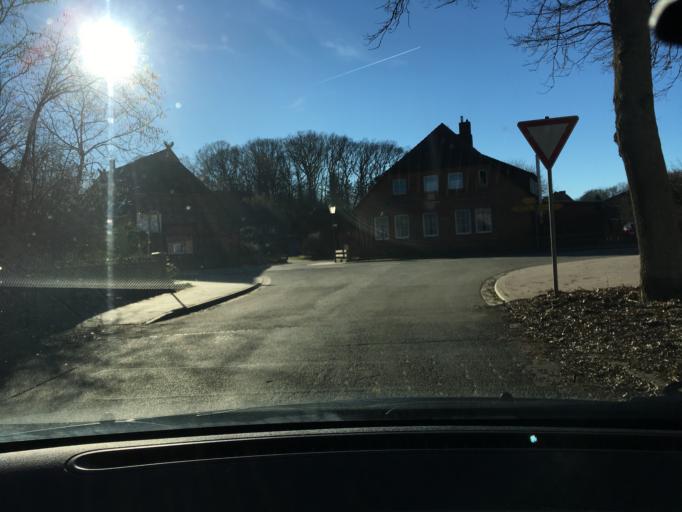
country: DE
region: Lower Saxony
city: Betzendorf
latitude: 53.1391
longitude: 10.3121
